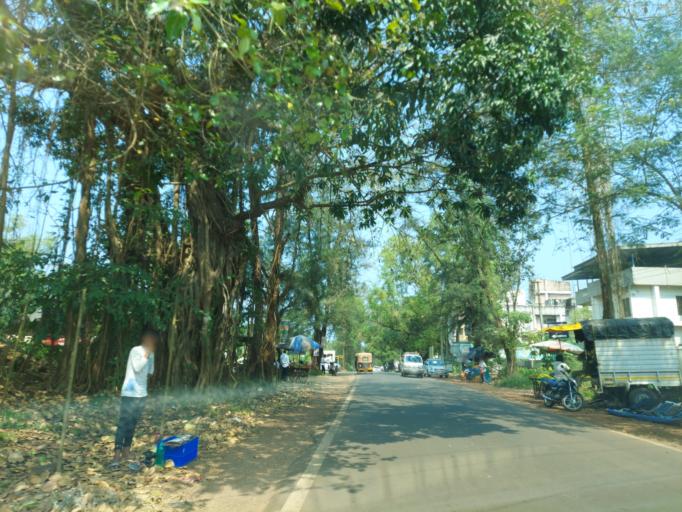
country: IN
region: Maharashtra
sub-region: Sindhudurg
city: Kudal
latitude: 15.9972
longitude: 73.6853
